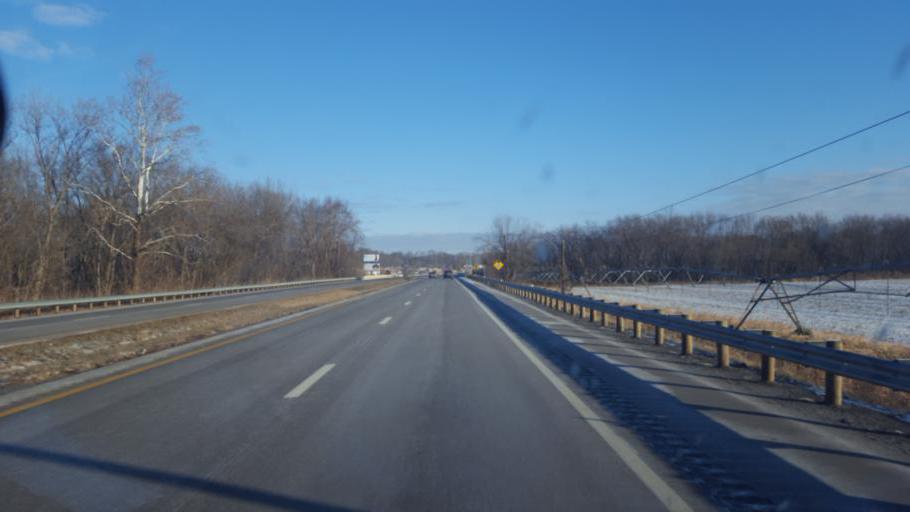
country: US
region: Ohio
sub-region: Pike County
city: Waverly
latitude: 39.1050
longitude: -82.9984
